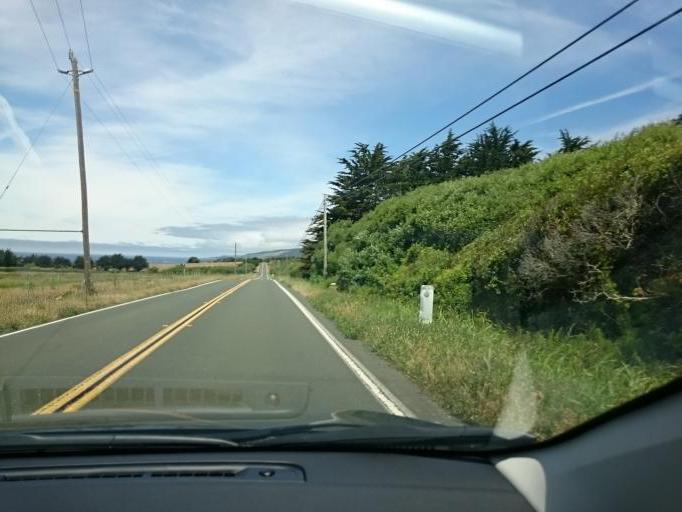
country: US
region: California
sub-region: Mendocino County
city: Boonville
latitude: 39.0946
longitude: -123.7033
